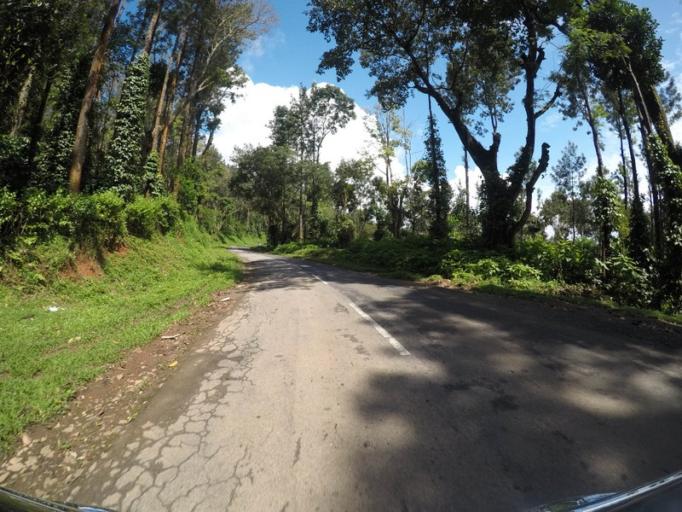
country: IN
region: Karnataka
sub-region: Kodagu
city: Suntikoppa
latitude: 12.5001
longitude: 75.8028
